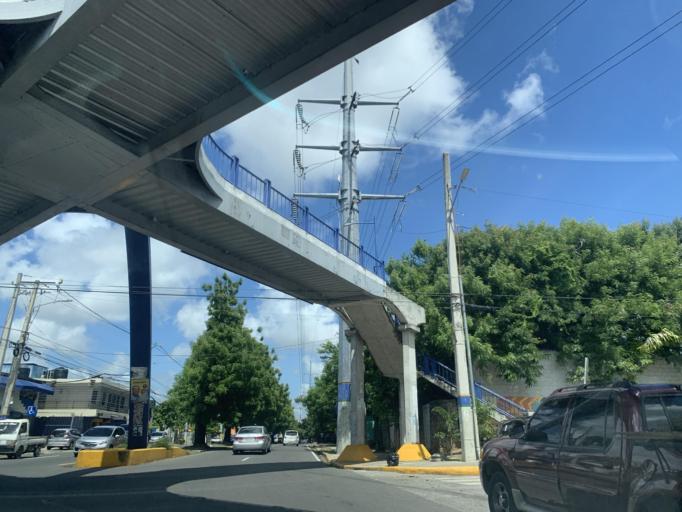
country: DO
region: Nacional
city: La Agustina
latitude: 18.5057
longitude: -69.9223
